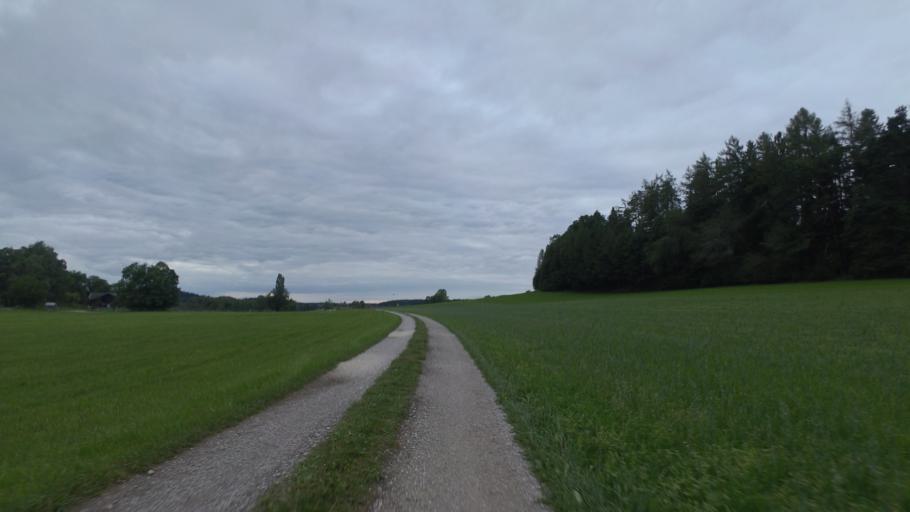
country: DE
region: Bavaria
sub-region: Upper Bavaria
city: Nussdorf
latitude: 47.9074
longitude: 12.5723
